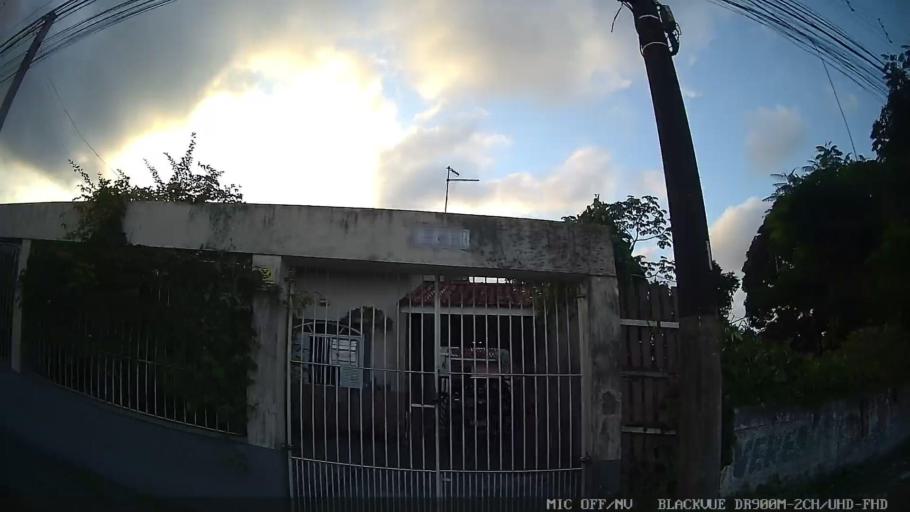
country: BR
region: Sao Paulo
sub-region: Peruibe
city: Peruibe
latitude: -24.3182
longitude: -47.0037
